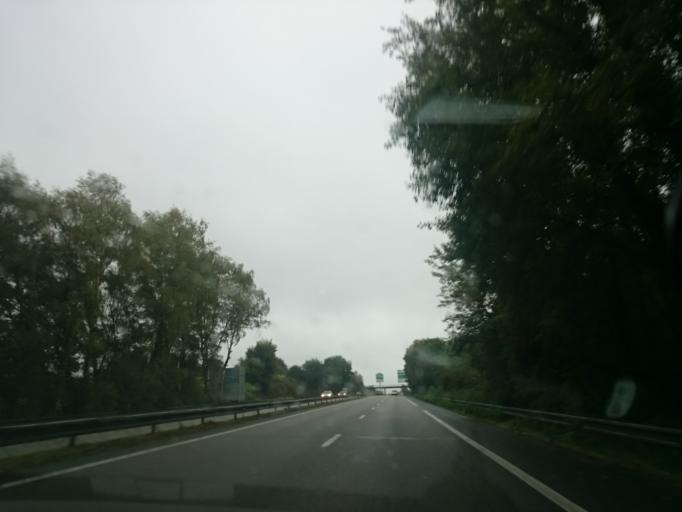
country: FR
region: Brittany
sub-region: Departement du Morbihan
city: Hennebont
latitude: 47.7890
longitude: -3.2565
